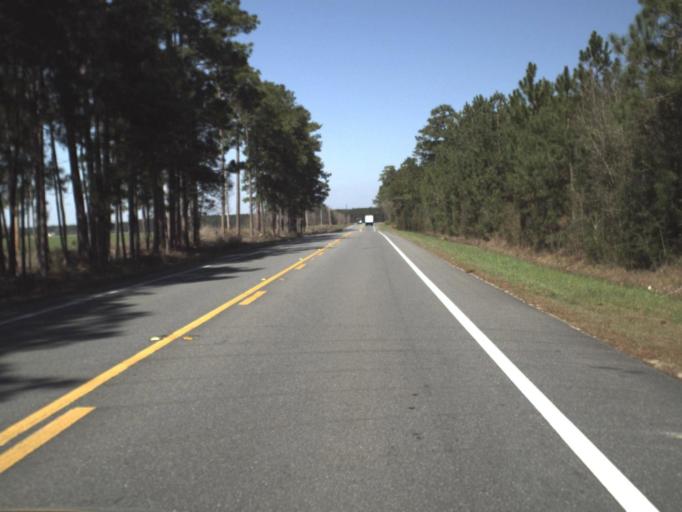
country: US
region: Florida
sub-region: Gulf County
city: Wewahitchka
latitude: 30.2046
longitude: -85.2088
